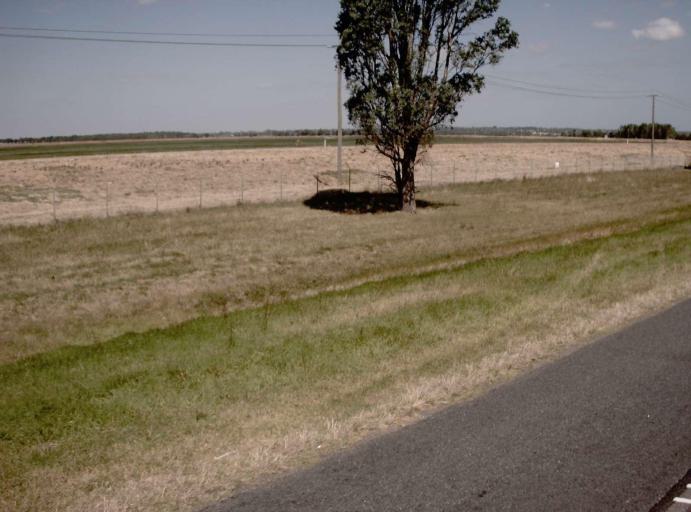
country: AU
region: Victoria
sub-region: Kingston
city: Patterson Lakes
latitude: -38.0613
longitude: 145.1484
